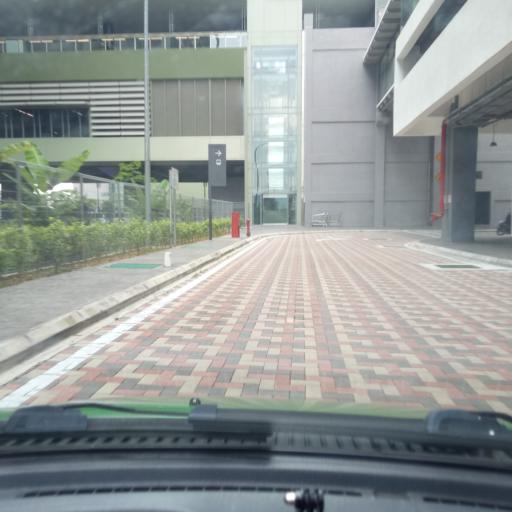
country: MY
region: Selangor
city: Kampong Baharu Balakong
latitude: 3.0013
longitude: 101.7844
